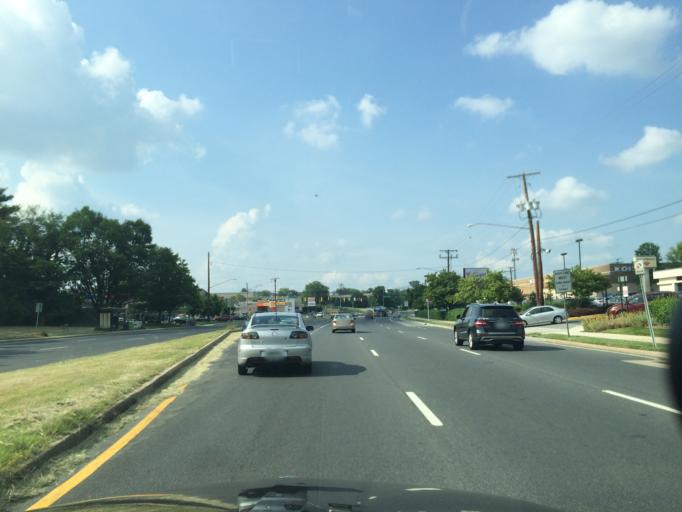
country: US
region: Maryland
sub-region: Montgomery County
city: Aspen Hill
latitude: 39.0785
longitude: -77.0807
